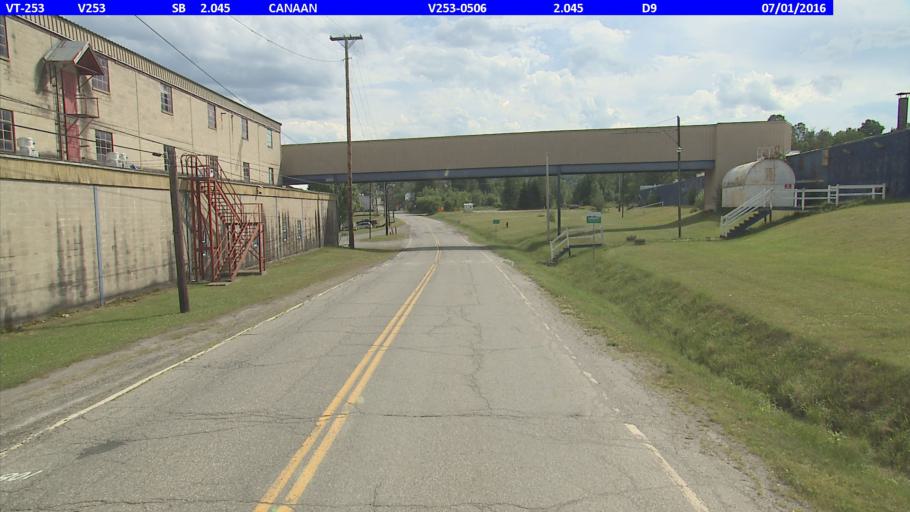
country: US
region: New Hampshire
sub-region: Coos County
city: Colebrook
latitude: 45.0120
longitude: -71.5061
